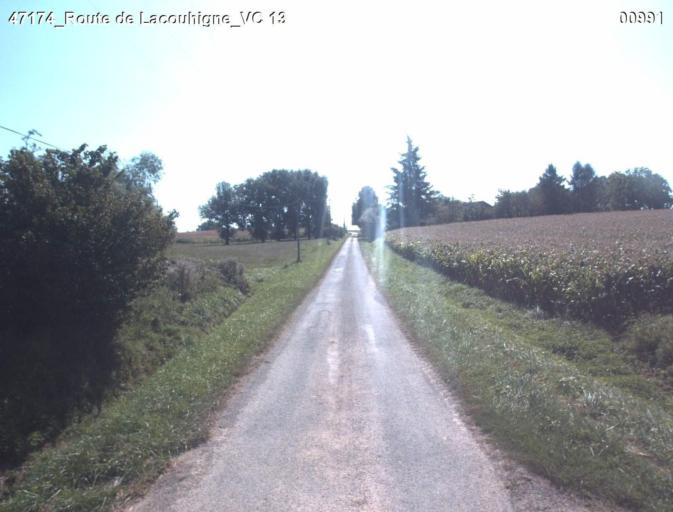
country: FR
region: Midi-Pyrenees
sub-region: Departement du Gers
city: Condom
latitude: 44.0220
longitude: 0.3816
